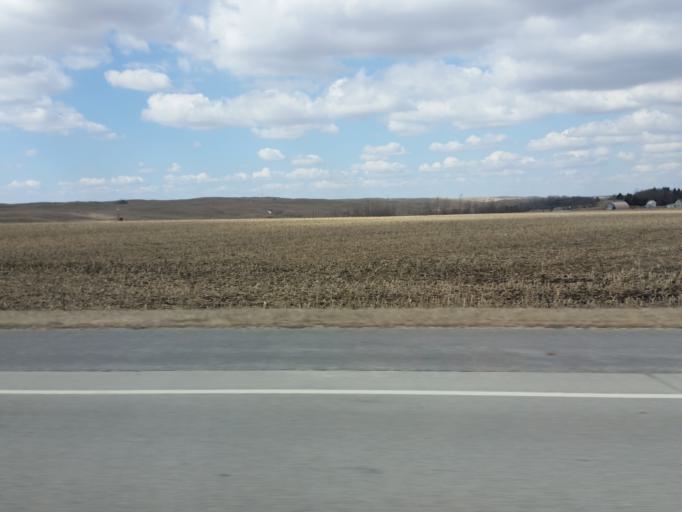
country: US
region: South Dakota
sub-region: Roberts County
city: Sisseton
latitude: 45.3871
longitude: -97.0380
